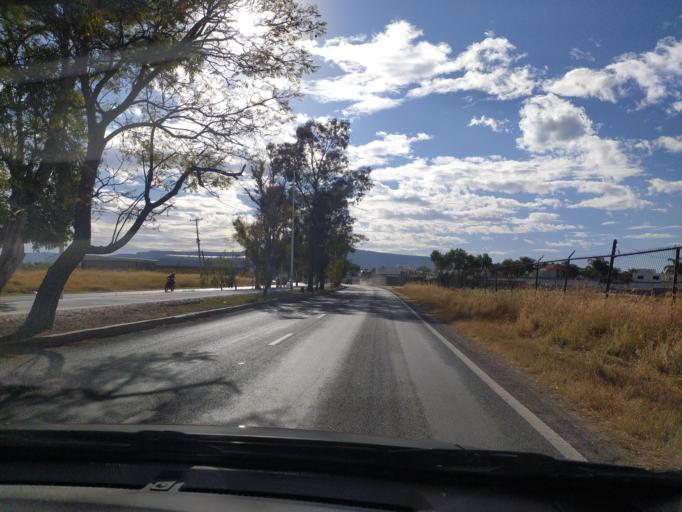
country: LA
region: Oudomxai
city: Muang La
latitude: 21.0320
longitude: 101.8401
